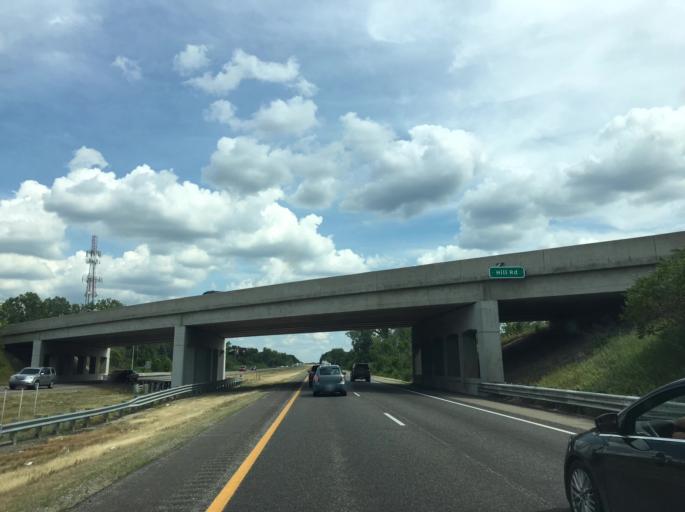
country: US
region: Michigan
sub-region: Genesee County
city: Flint
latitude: 42.9445
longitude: -83.7140
